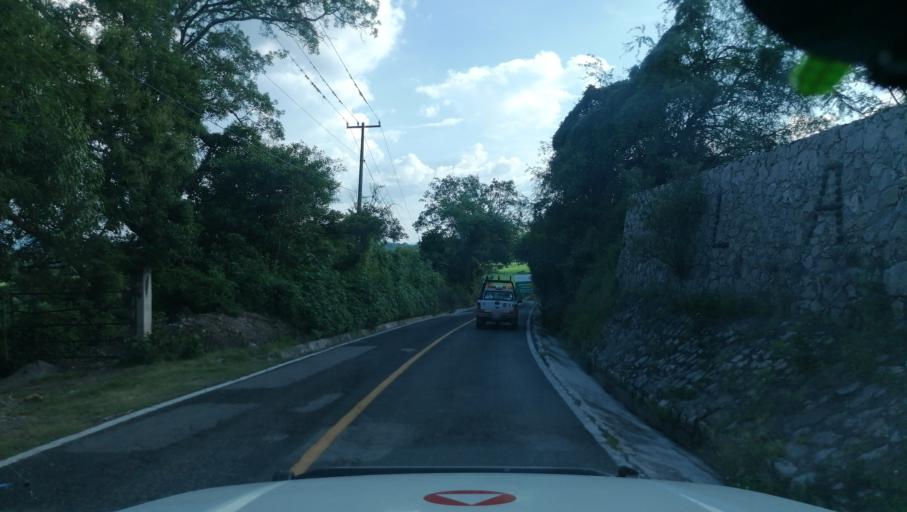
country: MX
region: Morelos
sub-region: Ayala
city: Abelardo L. Rodriguez
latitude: 18.7149
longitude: -98.9904
